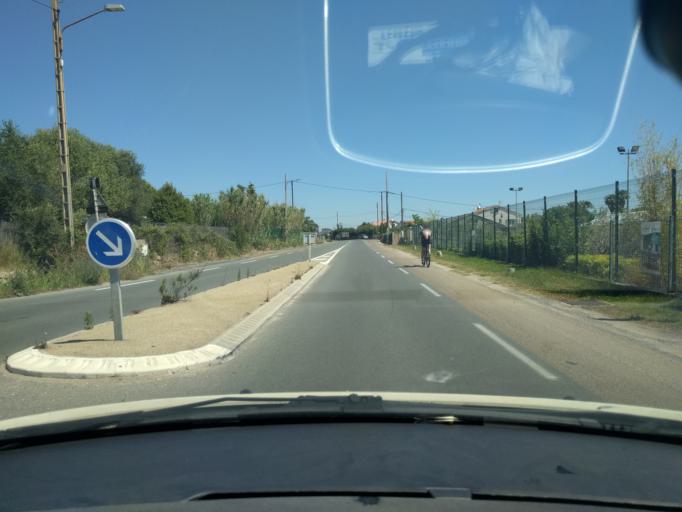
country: FR
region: Provence-Alpes-Cote d'Azur
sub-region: Departement du Var
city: Hyeres
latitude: 43.0826
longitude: 6.1285
